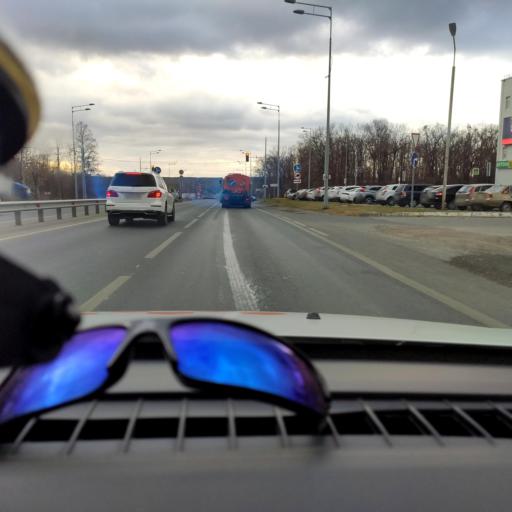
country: RU
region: Samara
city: Novosemeykino
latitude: 53.3475
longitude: 50.2334
